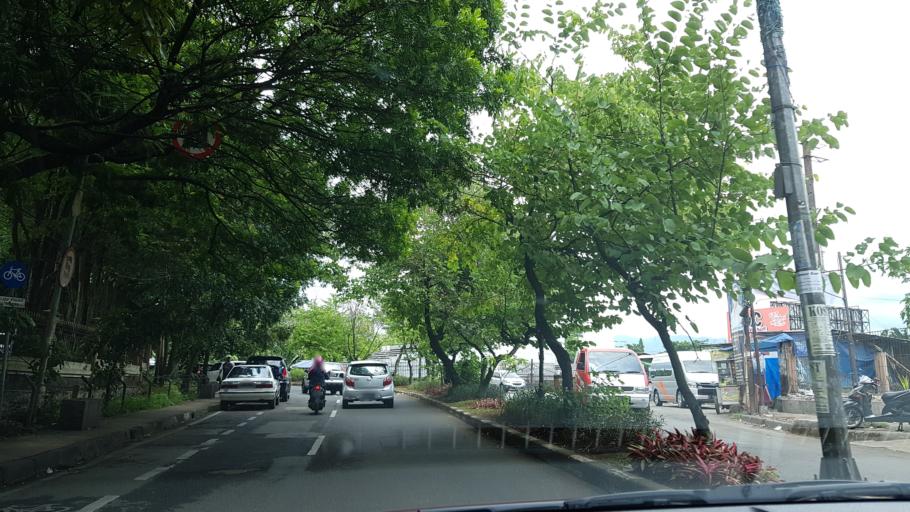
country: ID
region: West Java
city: Bandung
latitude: -6.8943
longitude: 107.6176
